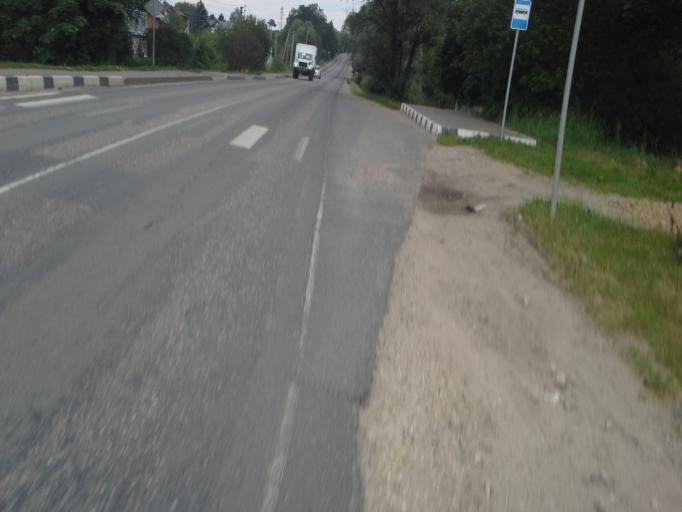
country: RU
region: Moskovskaya
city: Naro-Fominsk
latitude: 55.4078
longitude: 36.7923
